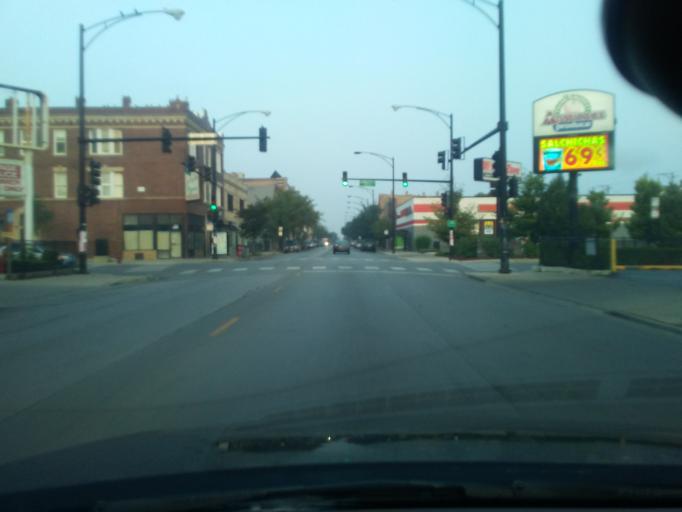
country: US
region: Illinois
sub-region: Cook County
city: Oak Park
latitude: 41.9174
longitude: -87.7115
